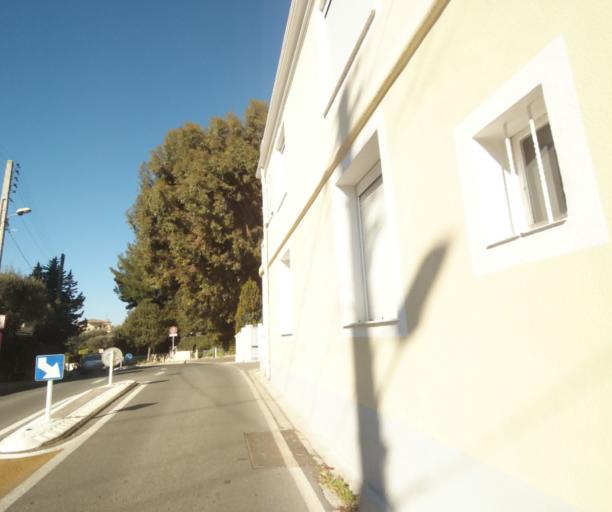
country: FR
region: Provence-Alpes-Cote d'Azur
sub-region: Departement des Alpes-Maritimes
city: Antibes
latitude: 43.5786
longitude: 7.1120
